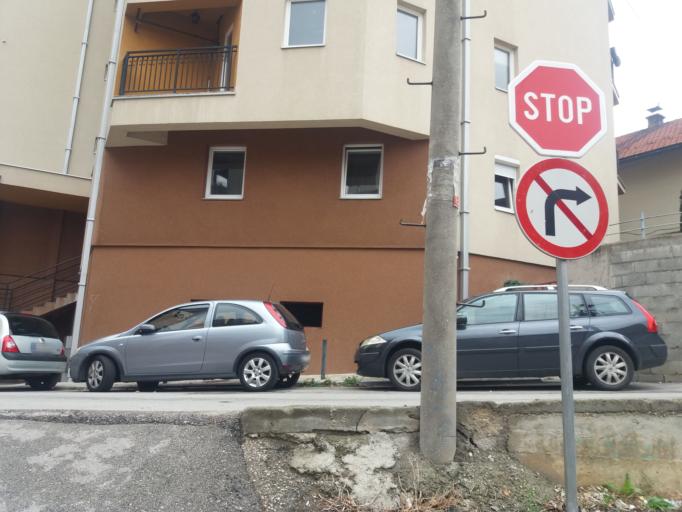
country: RS
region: Central Serbia
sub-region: Zlatiborski Okrug
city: Uzice
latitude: 43.8597
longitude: 19.8386
